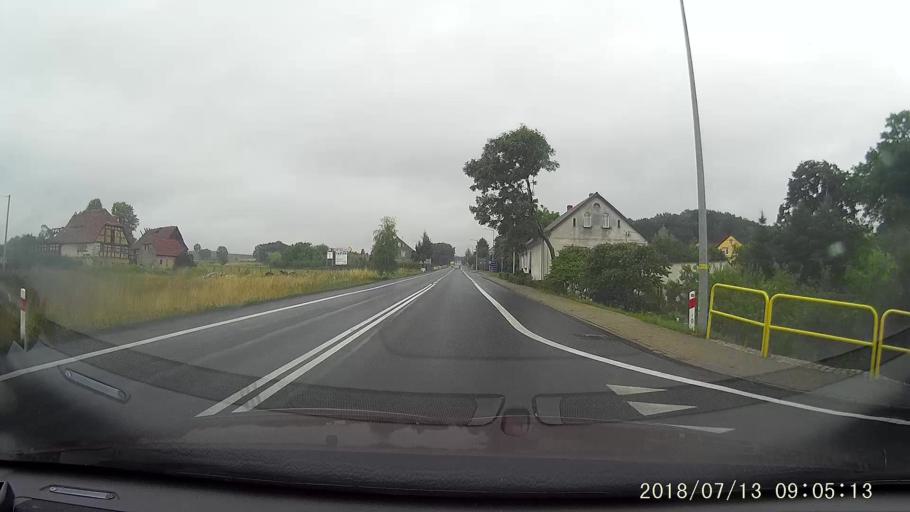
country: PL
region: Lower Silesian Voivodeship
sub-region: Powiat zgorzelecki
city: Lagow
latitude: 51.1560
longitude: 15.1222
